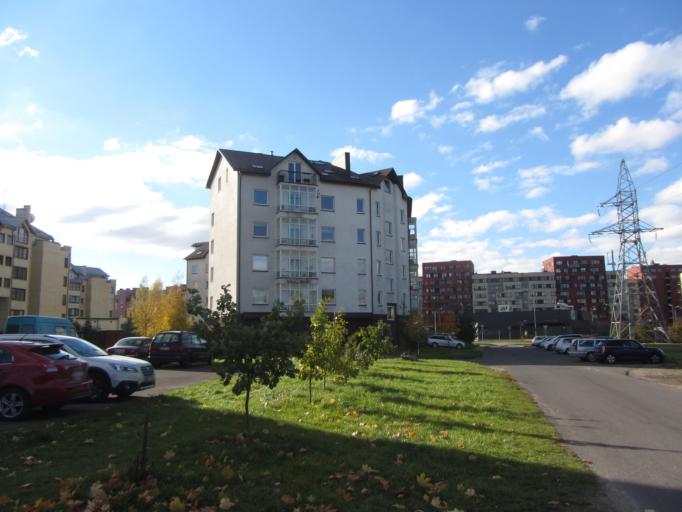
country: LT
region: Vilnius County
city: Lazdynai
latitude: 54.6666
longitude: 25.2175
